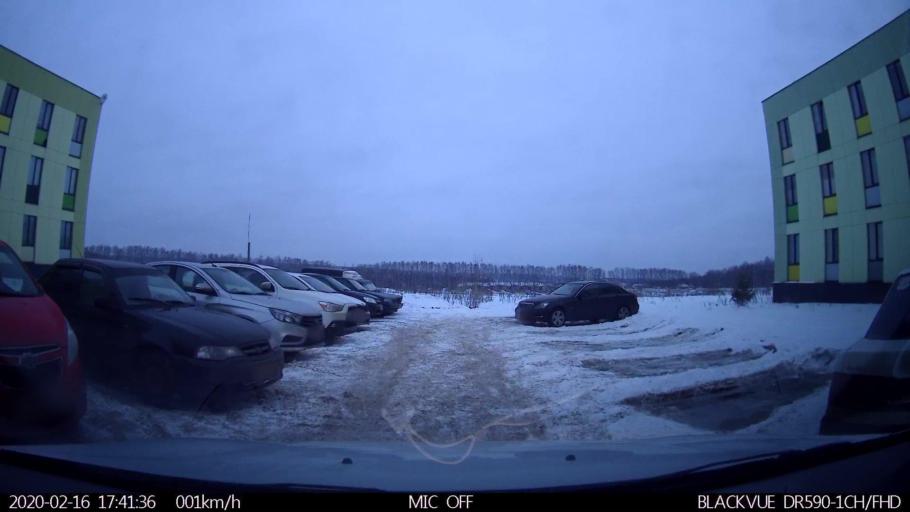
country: RU
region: Nizjnij Novgorod
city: Afonino
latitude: 56.2161
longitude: 44.0216
